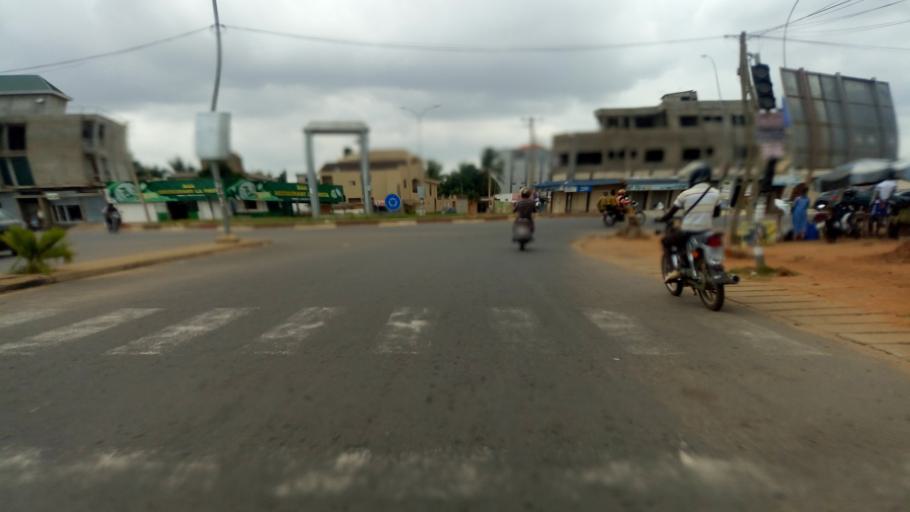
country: TG
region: Maritime
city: Lome
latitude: 6.2070
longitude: 1.1830
